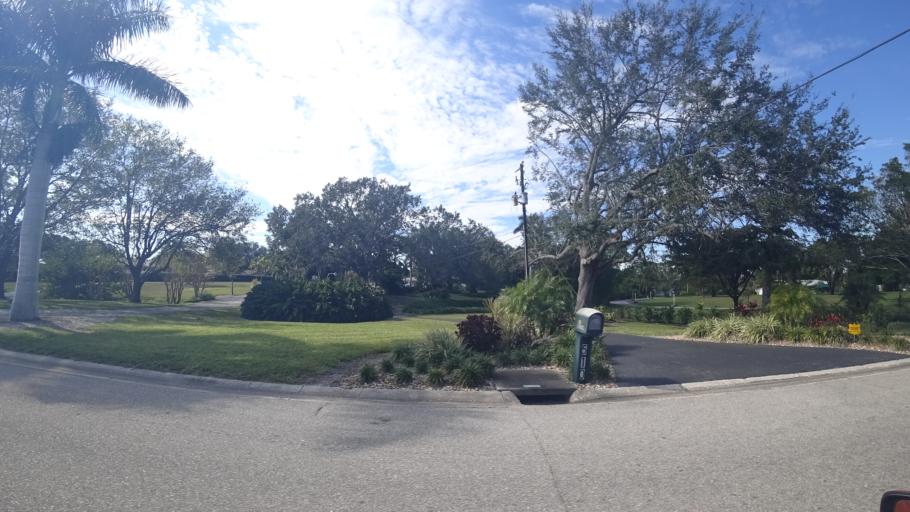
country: US
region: Florida
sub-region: Manatee County
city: West Bradenton
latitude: 27.5037
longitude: -82.6242
